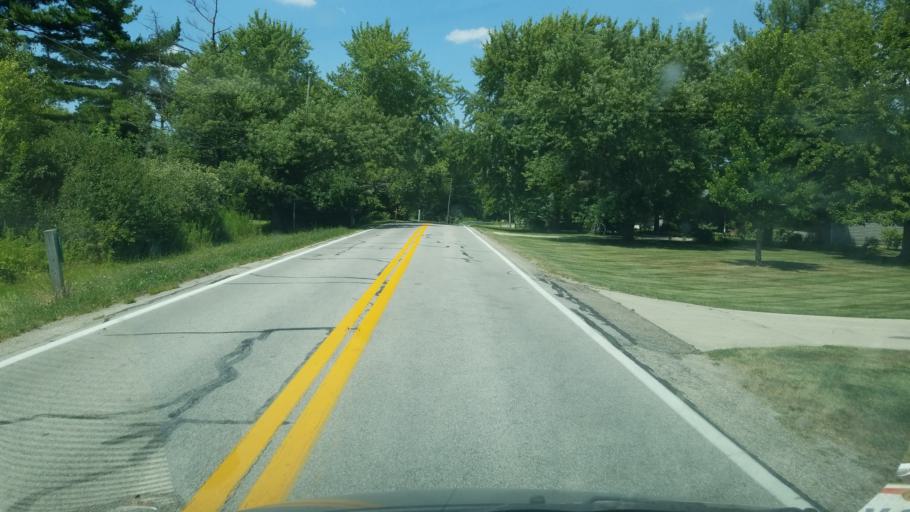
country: US
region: Ohio
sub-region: Franklin County
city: Lake Darby
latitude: 39.9933
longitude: -83.2460
